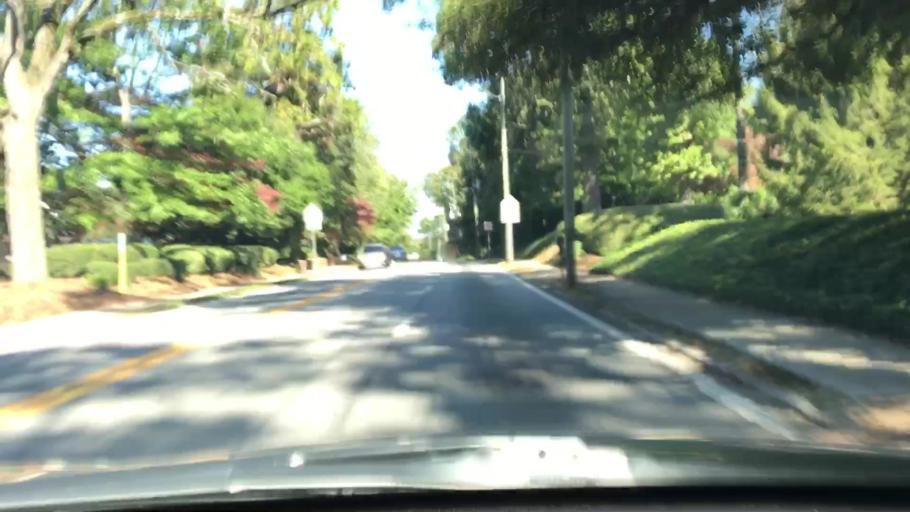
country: US
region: Georgia
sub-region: DeKalb County
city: Decatur
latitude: 33.7686
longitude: -84.2926
